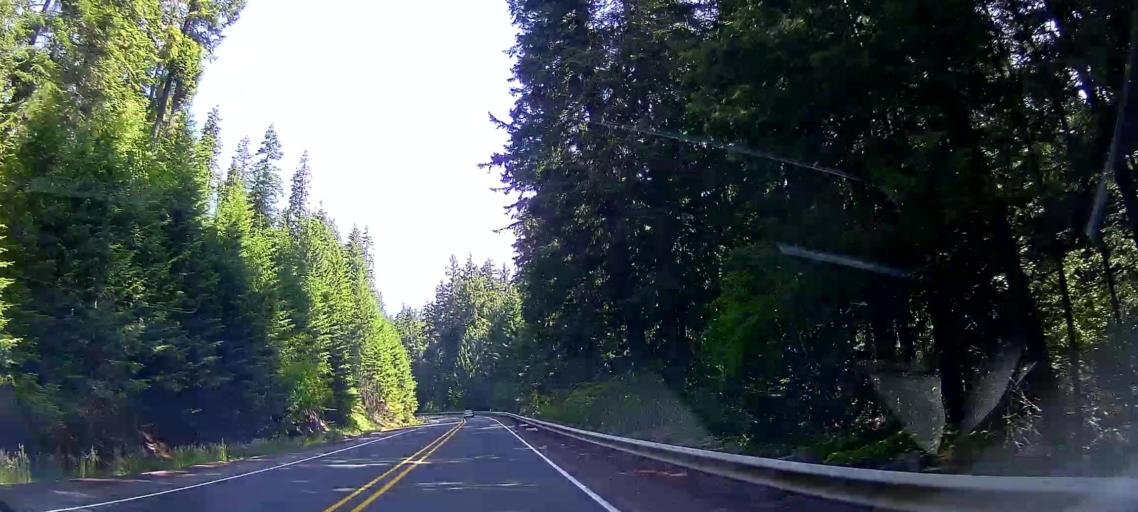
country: US
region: Oregon
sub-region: Jefferson County
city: Warm Springs
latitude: 45.0998
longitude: -121.5520
